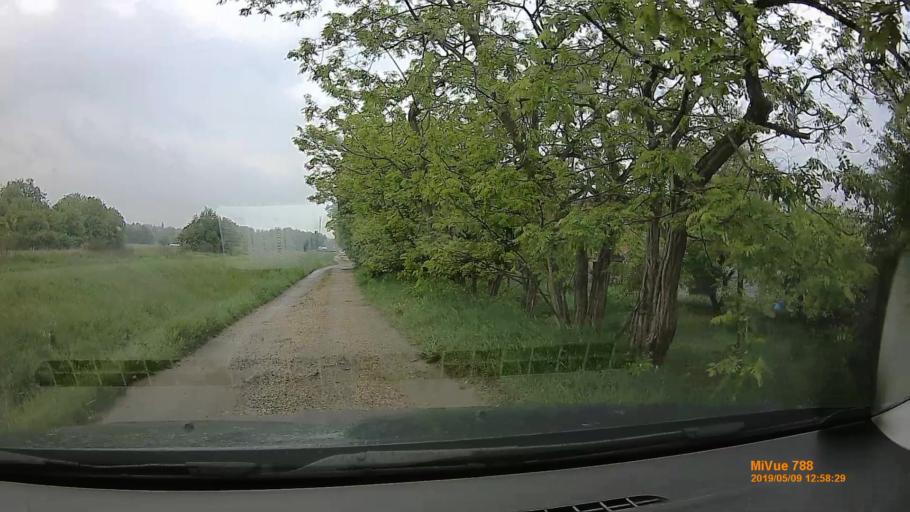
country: HU
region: Budapest
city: Budapest XVI. keruelet
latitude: 47.5376
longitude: 19.1724
